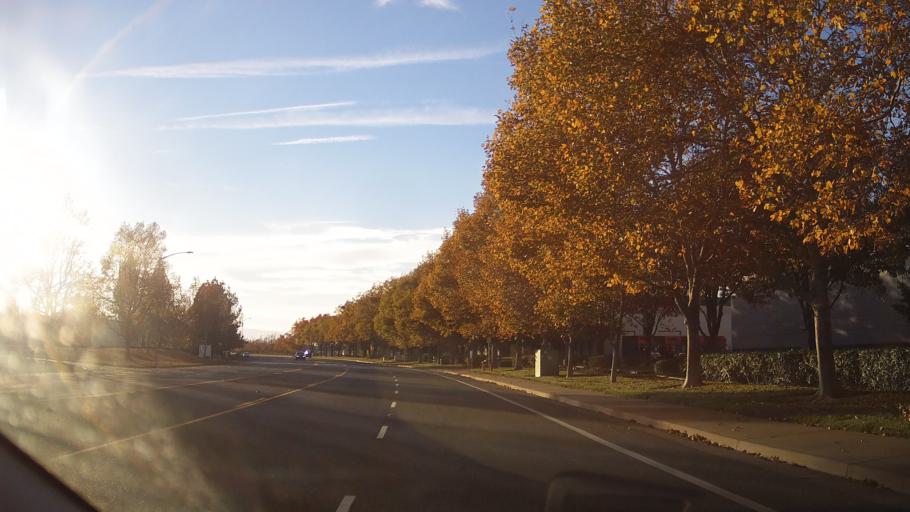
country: US
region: California
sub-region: Yolo County
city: West Sacramento
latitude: 38.5736
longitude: -121.5640
